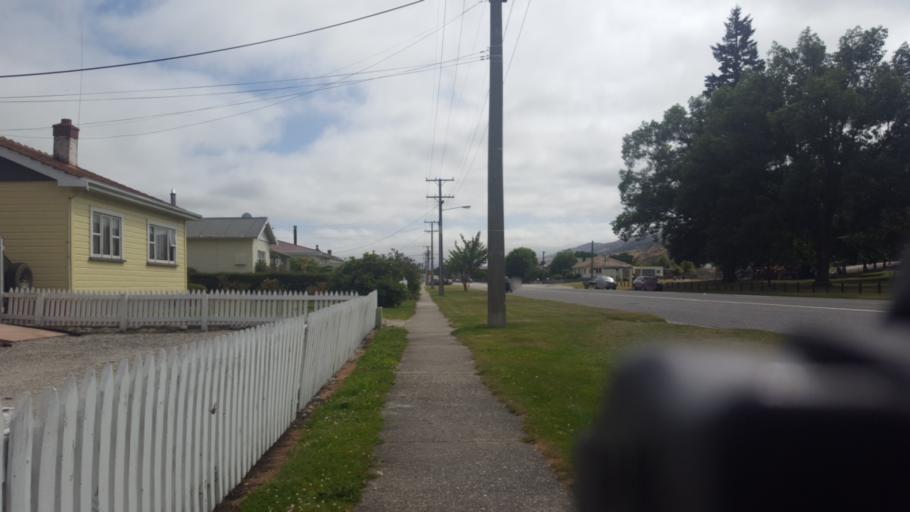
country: NZ
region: Otago
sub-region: Queenstown-Lakes District
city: Kingston
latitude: -45.5451
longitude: 169.3134
